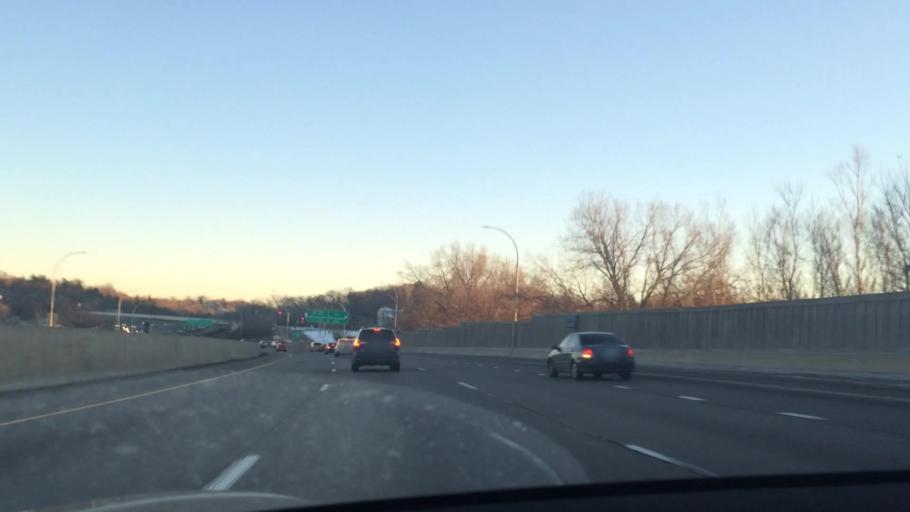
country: US
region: Minnesota
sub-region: Hennepin County
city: Golden Valley
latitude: 44.9802
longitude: -93.3482
